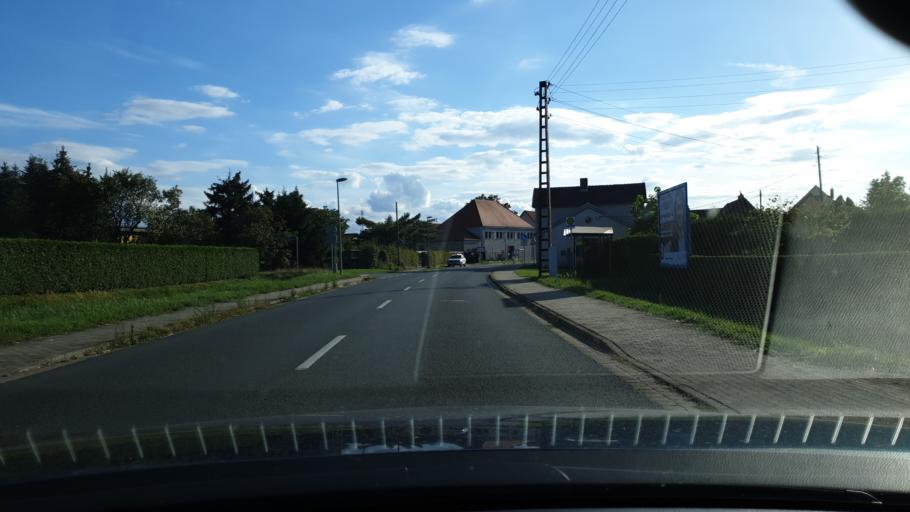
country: DE
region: Saxony-Anhalt
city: Radis
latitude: 51.7526
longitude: 12.5185
